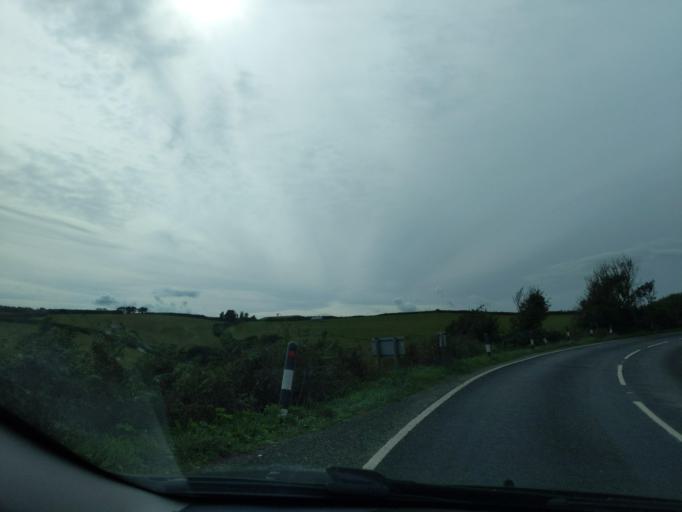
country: GB
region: England
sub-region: Cornwall
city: Mevagissey
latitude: 50.2842
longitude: -4.7862
